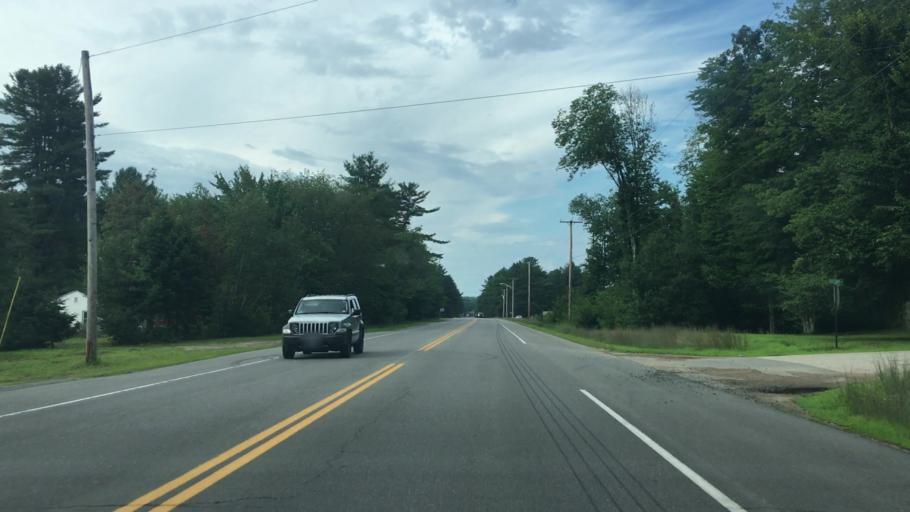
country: US
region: New Hampshire
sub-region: Strafford County
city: Rochester
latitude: 43.3455
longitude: -70.9330
